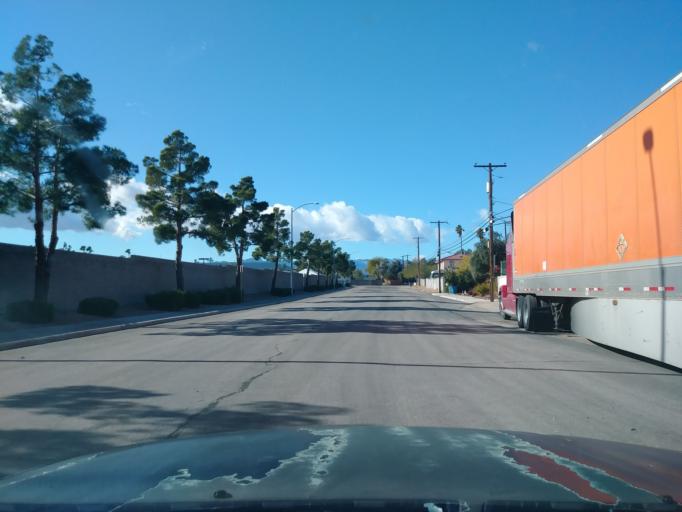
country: US
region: Nevada
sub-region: Clark County
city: Spring Valley
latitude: 36.1462
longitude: -115.2191
